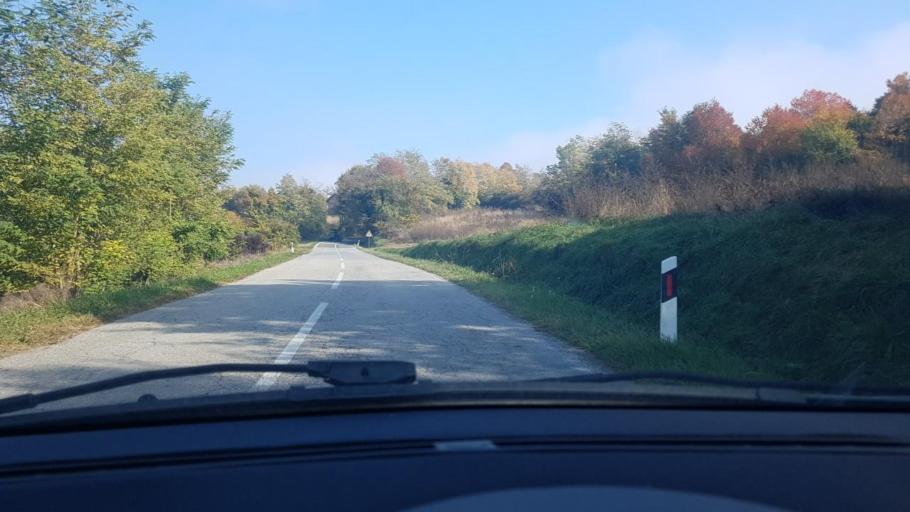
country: HR
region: Krapinsko-Zagorska
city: Zlatar
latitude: 46.1345
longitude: 16.1272
